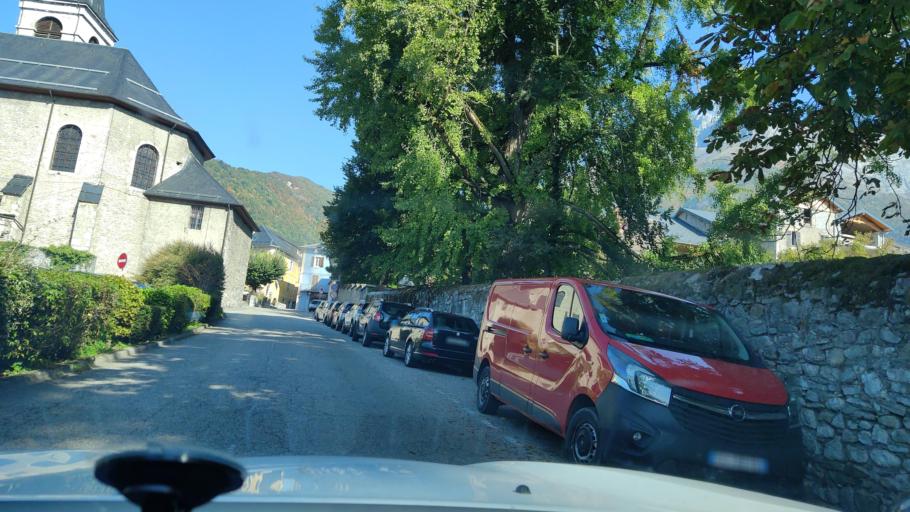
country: FR
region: Rhone-Alpes
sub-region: Departement de la Savoie
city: Coise-Saint-Jean-Pied-Gauthier
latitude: 45.5685
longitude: 6.1548
